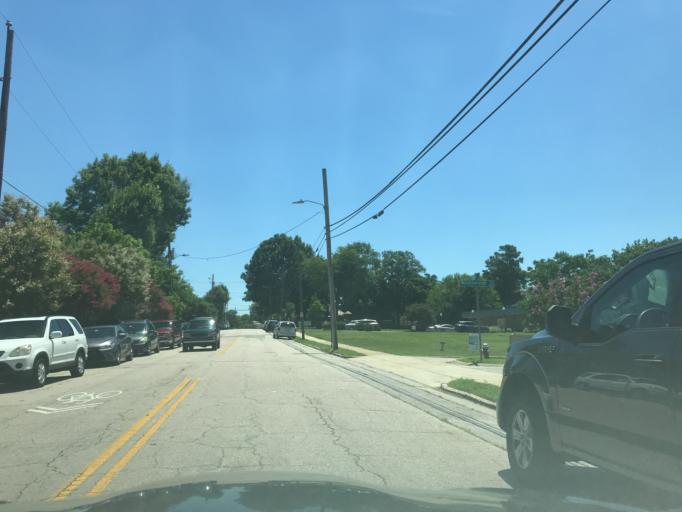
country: US
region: North Carolina
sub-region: Wake County
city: Raleigh
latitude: 35.7780
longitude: -78.6311
